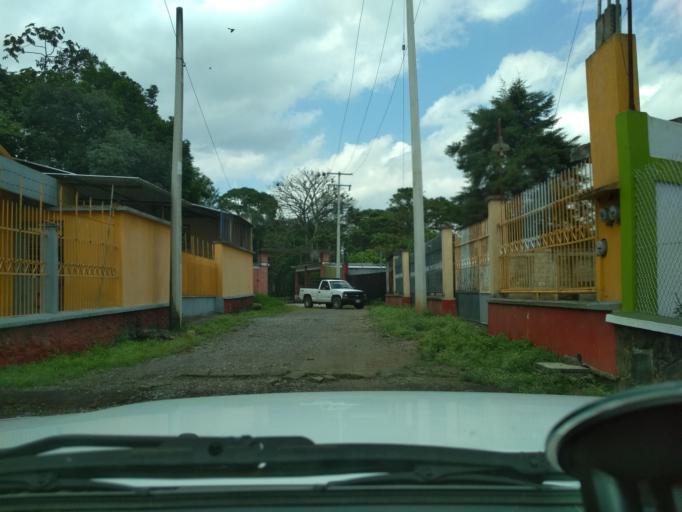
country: MX
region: Veracruz
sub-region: Fortin
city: Monte Salas
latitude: 18.9349
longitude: -97.0165
